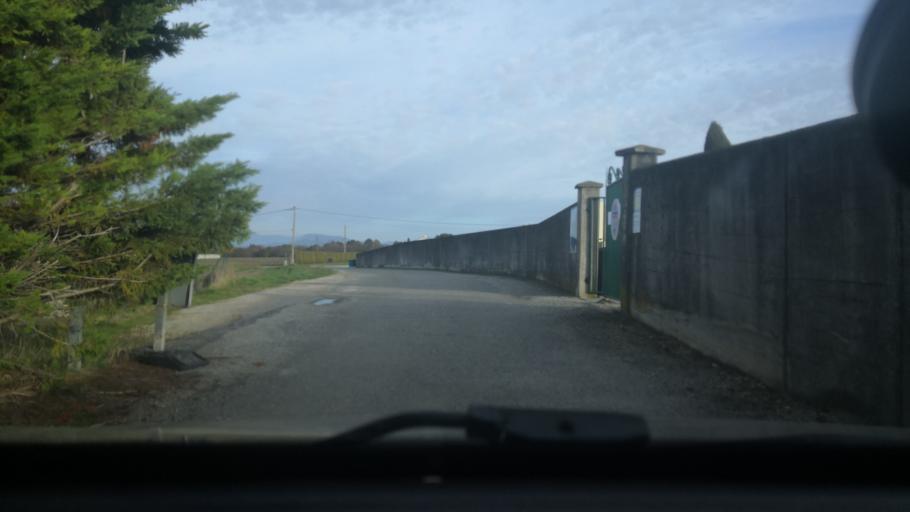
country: FR
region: Rhone-Alpes
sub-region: Departement de la Drome
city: Montelimar
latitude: 44.5404
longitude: 4.7721
